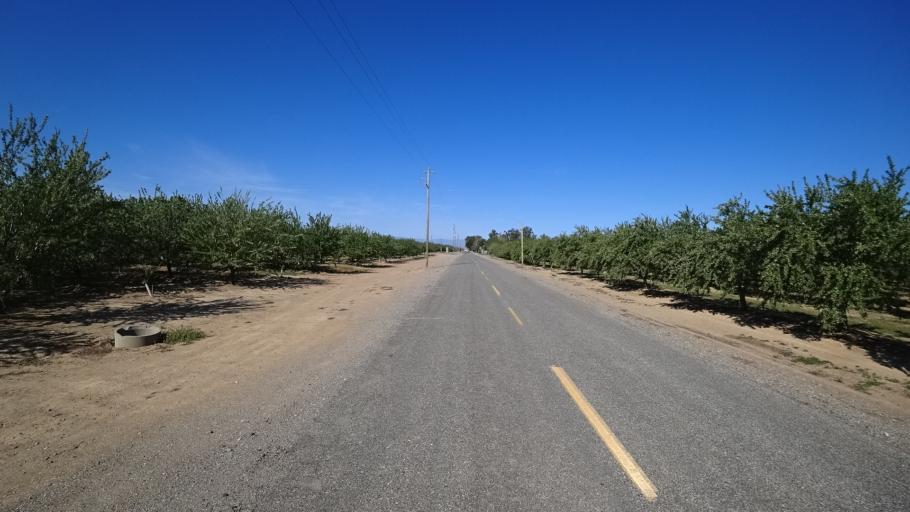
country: US
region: California
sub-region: Glenn County
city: Willows
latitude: 39.6113
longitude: -122.1819
